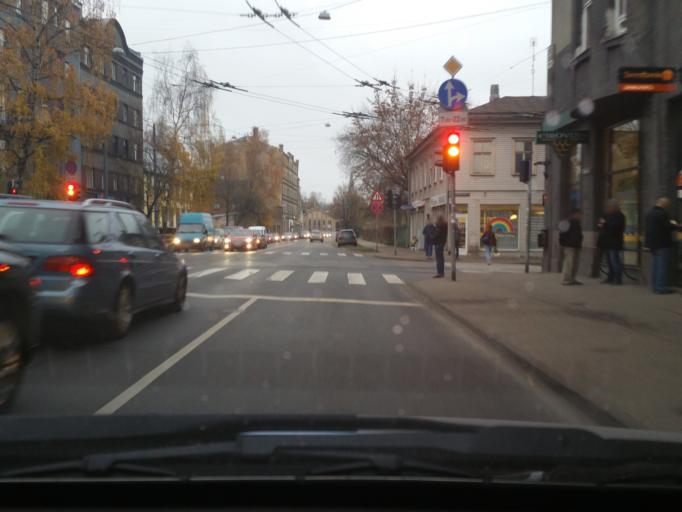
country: LV
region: Riga
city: Riga
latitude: 56.9502
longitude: 24.1324
